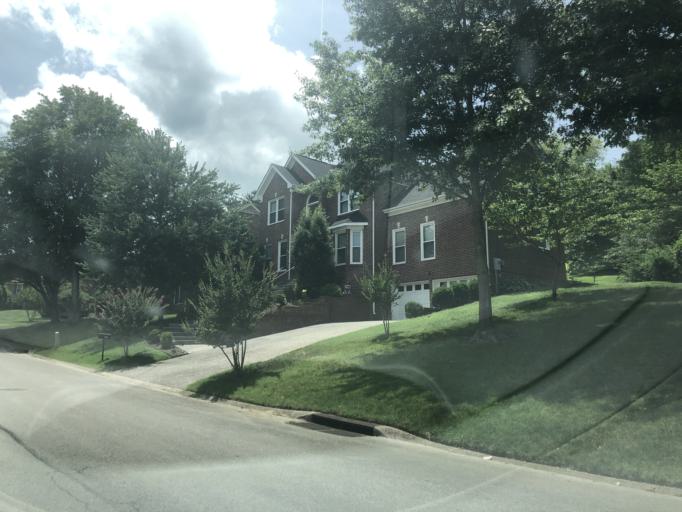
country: US
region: Tennessee
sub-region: Davidson County
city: Belle Meade
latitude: 36.0512
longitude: -86.9548
